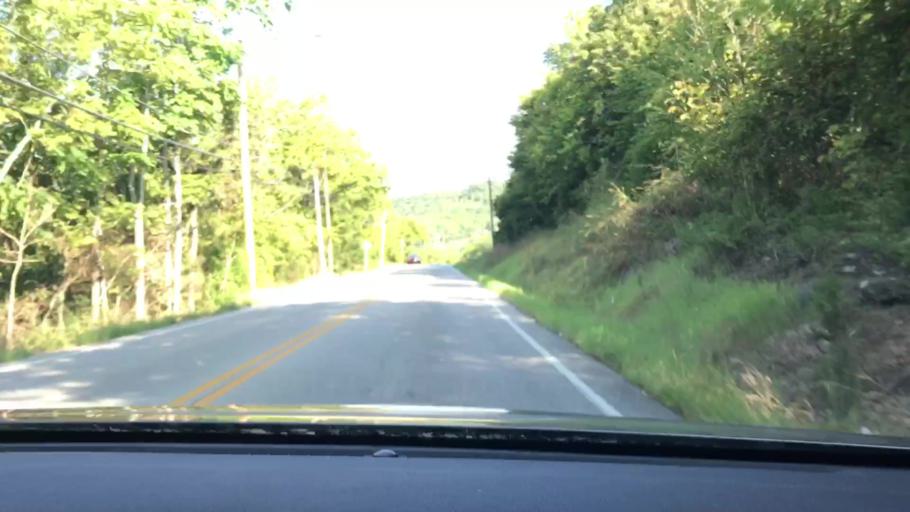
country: US
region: Tennessee
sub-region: Smith County
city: Carthage
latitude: 36.2640
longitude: -85.9548
